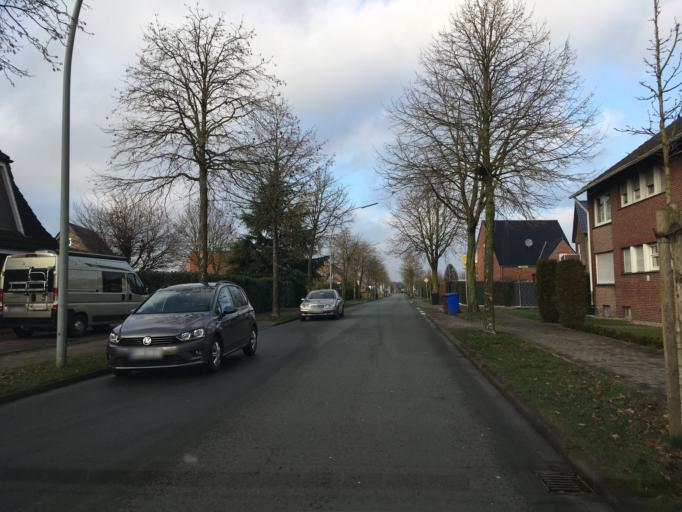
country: DE
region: North Rhine-Westphalia
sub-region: Regierungsbezirk Munster
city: Gescher
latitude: 51.9581
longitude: 6.9917
